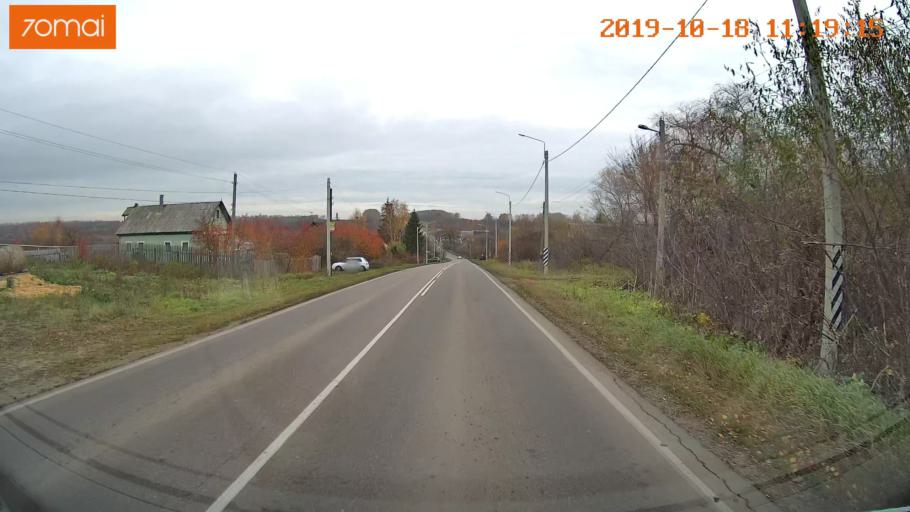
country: RU
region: Tula
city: Kimovsk
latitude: 54.0445
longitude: 38.5528
